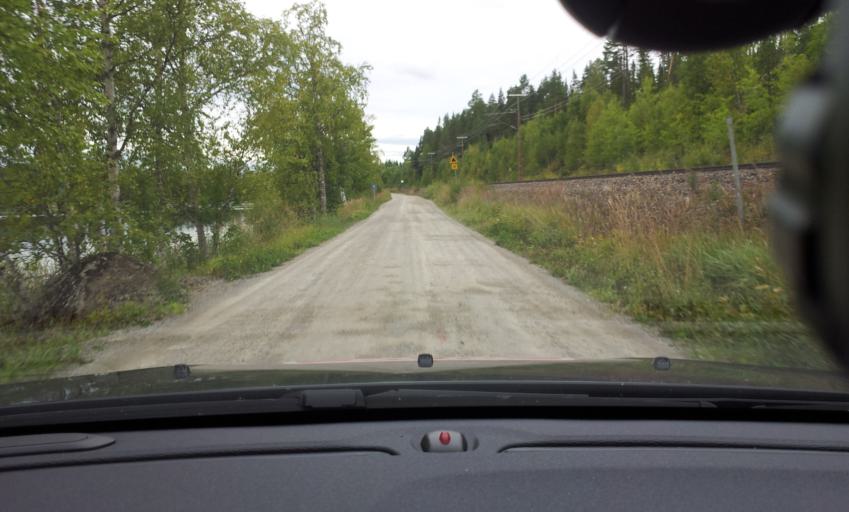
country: SE
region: Jaemtland
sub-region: OEstersunds Kommun
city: Brunflo
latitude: 62.9823
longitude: 14.9866
